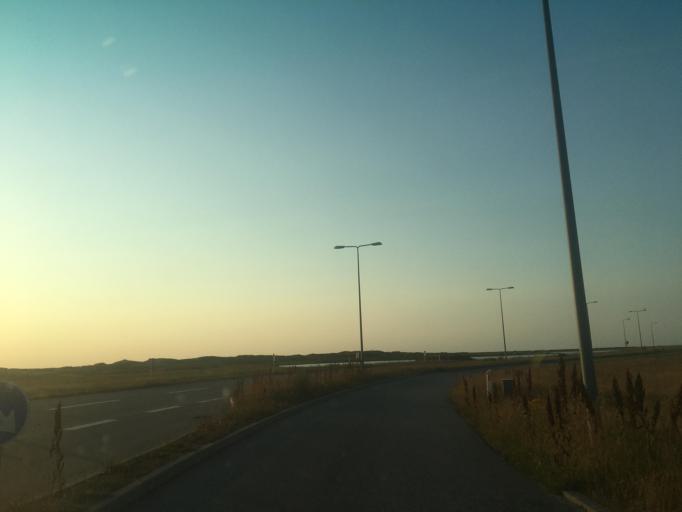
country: DK
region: Central Jutland
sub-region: Lemvig Kommune
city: Thyboron
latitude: 56.7029
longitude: 8.2454
